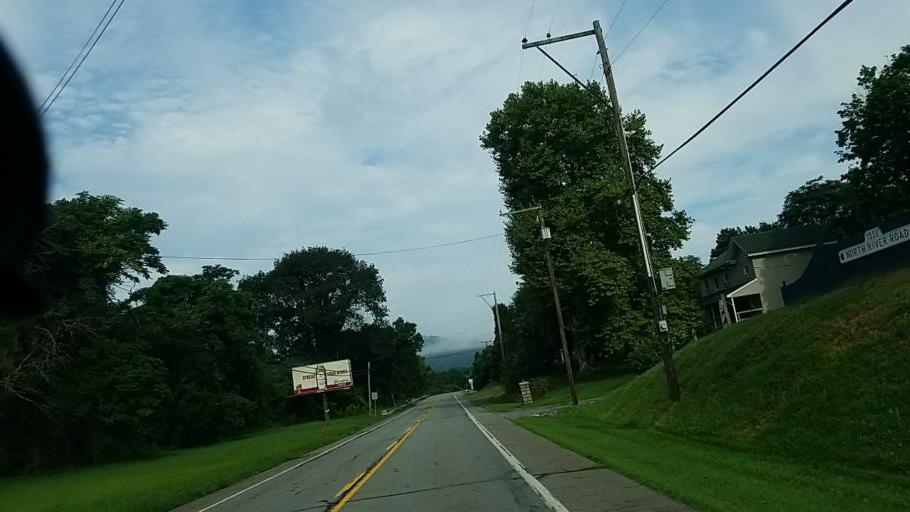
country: US
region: Pennsylvania
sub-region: Dauphin County
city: Millersburg
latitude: 40.5079
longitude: -76.9601
